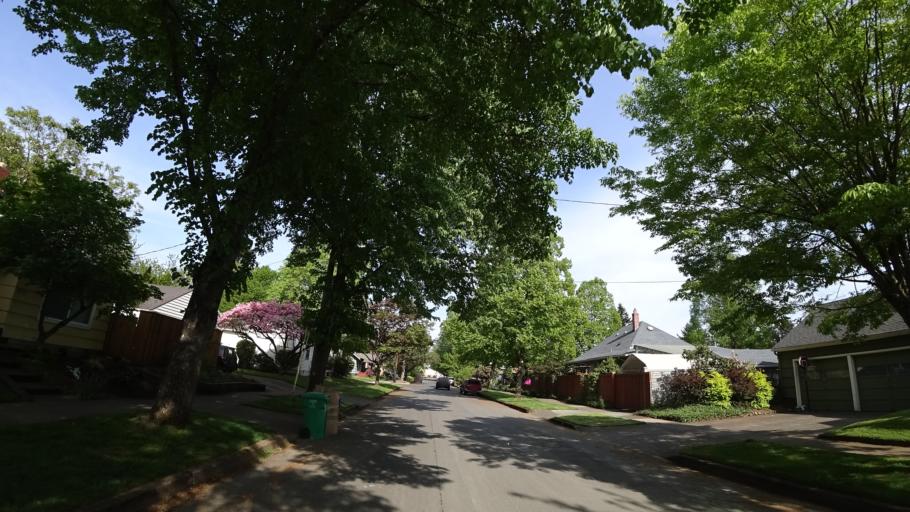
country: US
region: Oregon
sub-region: Clackamas County
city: Milwaukie
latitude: 45.4778
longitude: -122.6121
